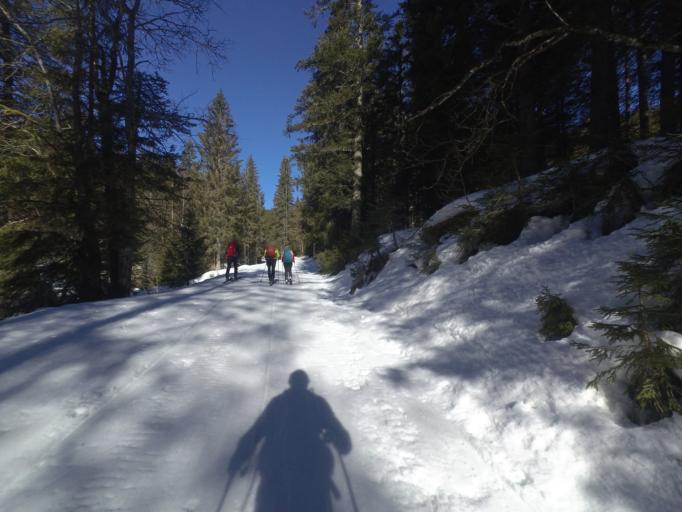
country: AT
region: Upper Austria
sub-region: Politischer Bezirk Gmunden
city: Sankt Wolfgang im Salzkammergut
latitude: 47.6498
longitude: 13.4137
